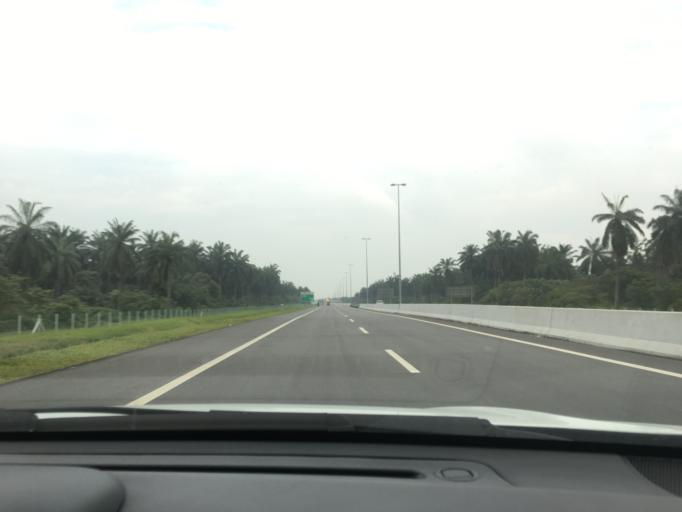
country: MY
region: Selangor
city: Klang
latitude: 3.1170
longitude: 101.4103
